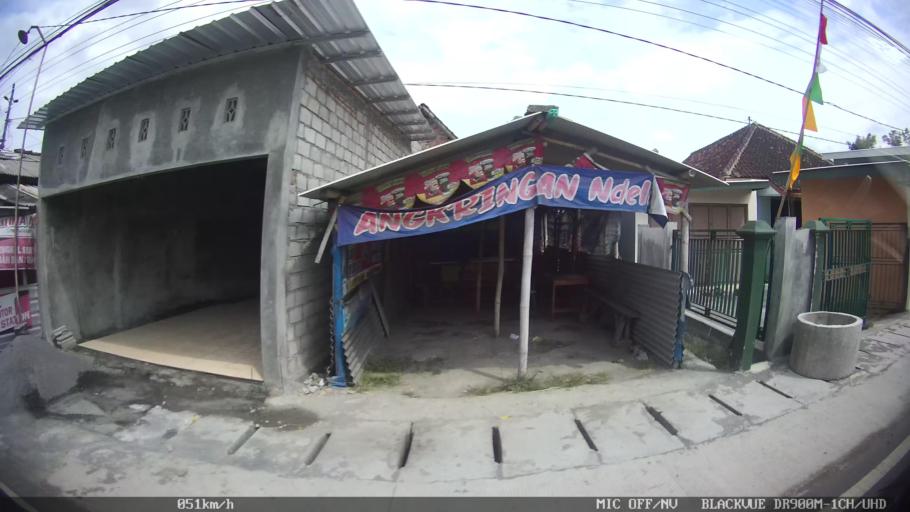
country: ID
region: Central Java
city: Candi Prambanan
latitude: -7.7955
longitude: 110.4827
